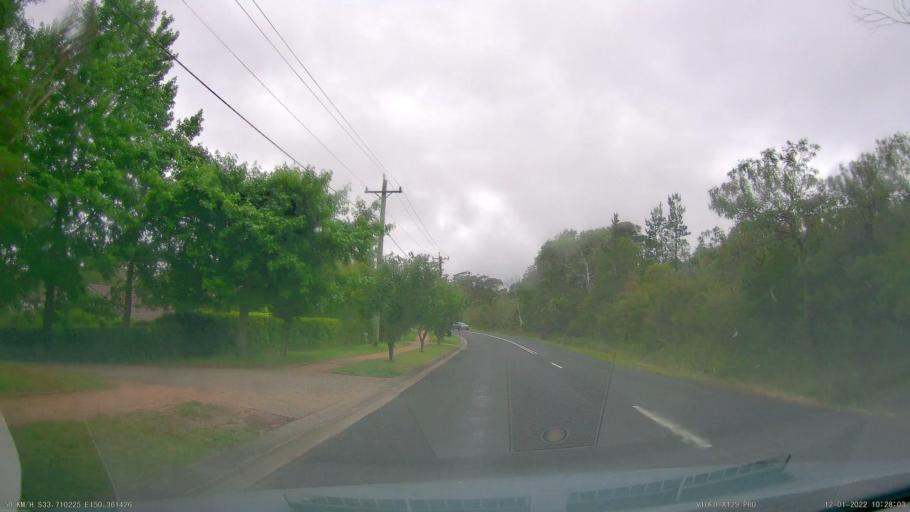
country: AU
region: New South Wales
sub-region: Blue Mountains Municipality
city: Leura
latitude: -33.7102
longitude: 150.3617
